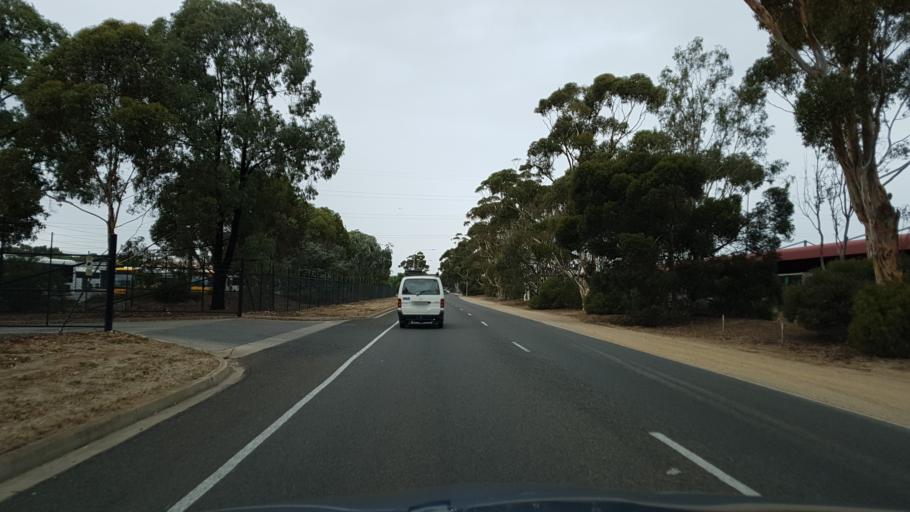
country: AU
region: South Australia
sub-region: Port Adelaide Enfield
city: Enfield
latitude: -34.8293
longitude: 138.6072
